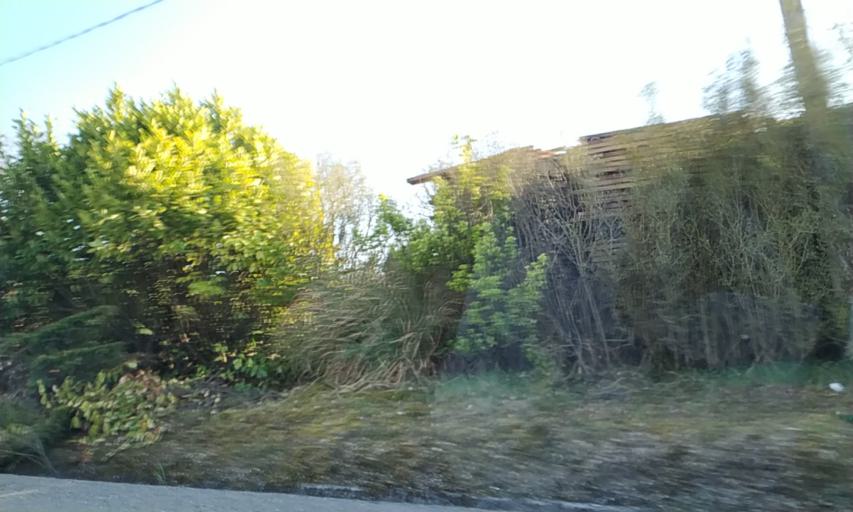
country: ES
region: Galicia
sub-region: Provincia de Lugo
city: Corgo
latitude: 42.9581
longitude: -7.4723
